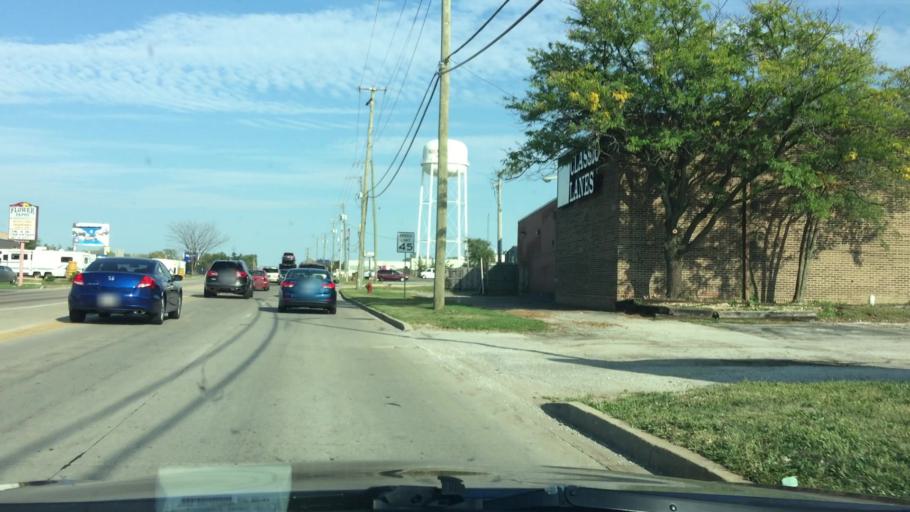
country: US
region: Illinois
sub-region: Cook County
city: South Chicago Heights
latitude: 41.4812
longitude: -87.6327
